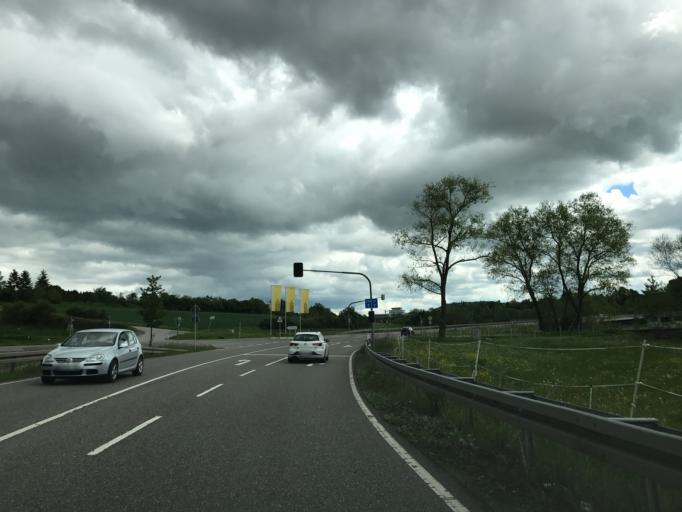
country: DE
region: Baden-Wuerttemberg
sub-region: Regierungsbezirk Stuttgart
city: Leonberg
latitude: 48.7914
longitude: 8.9842
